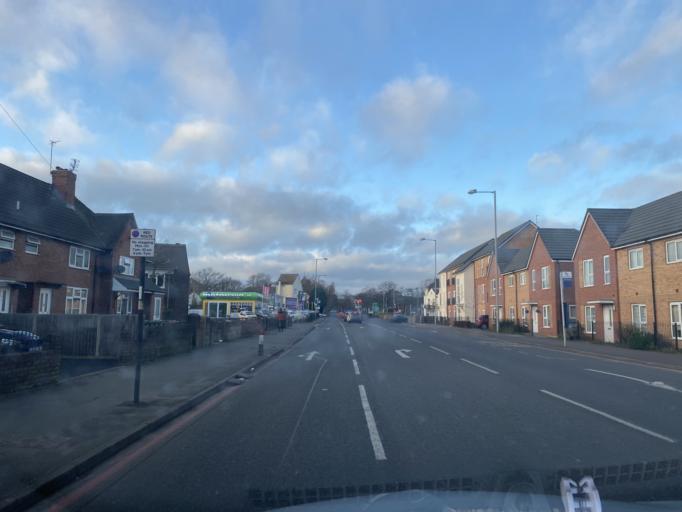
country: GB
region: England
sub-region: Walsall
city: Bloxwich
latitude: 52.6122
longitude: -2.0029
